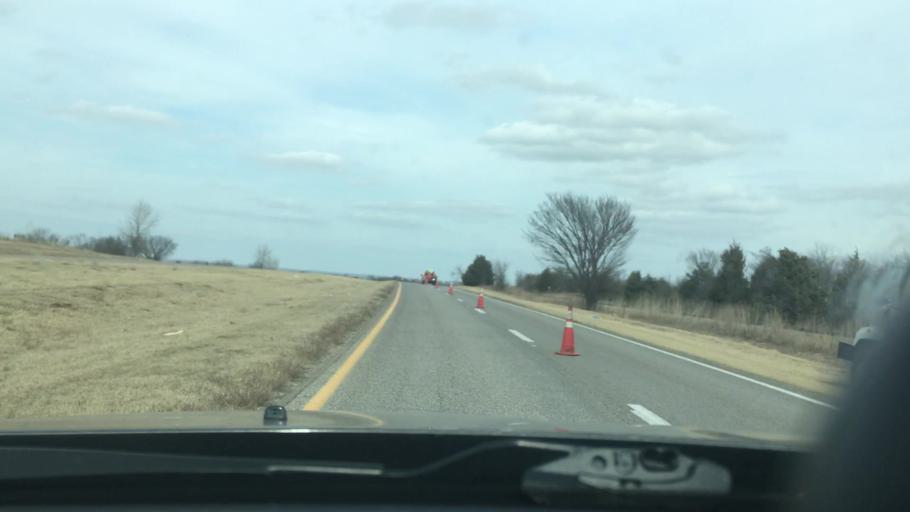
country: US
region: Oklahoma
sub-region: Pontotoc County
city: Ada
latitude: 34.7050
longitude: -96.7314
